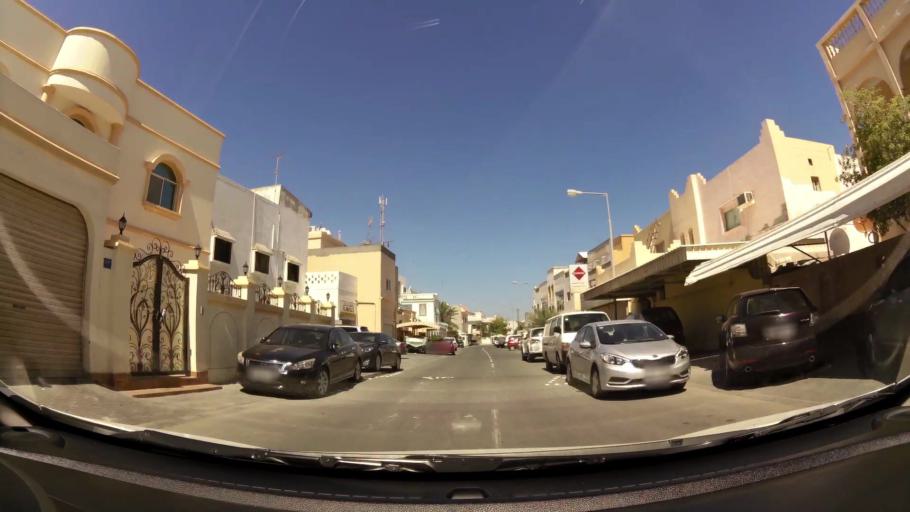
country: BH
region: Muharraq
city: Al Muharraq
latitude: 26.2678
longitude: 50.6059
